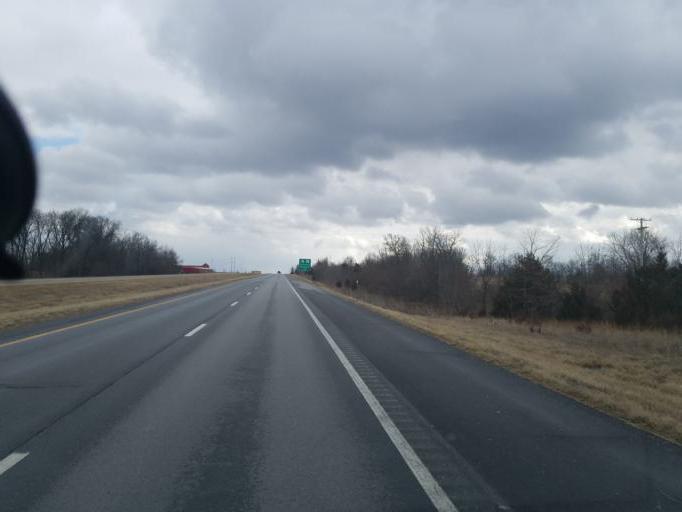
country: US
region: Missouri
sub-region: Boone County
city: Hallsville
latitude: 39.2615
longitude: -92.3344
